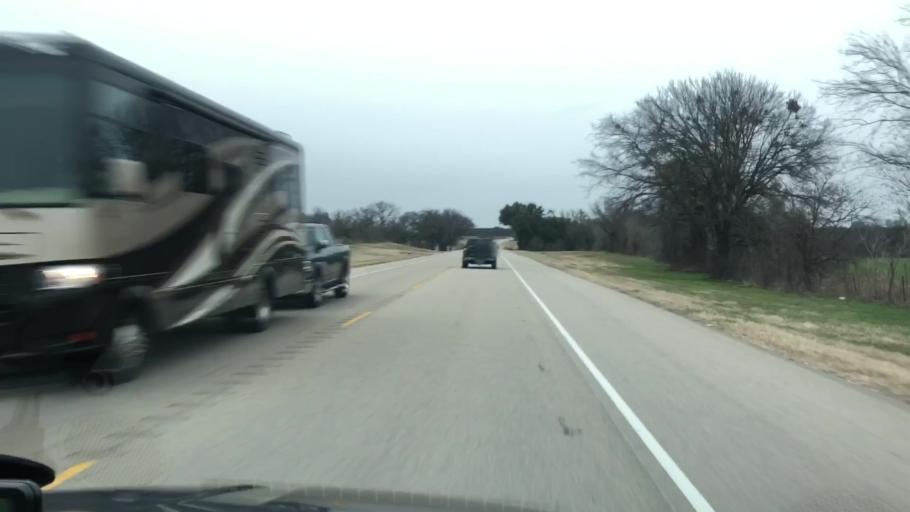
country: US
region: Texas
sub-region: Hamilton County
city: Hamilton
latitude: 31.6061
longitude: -98.1583
